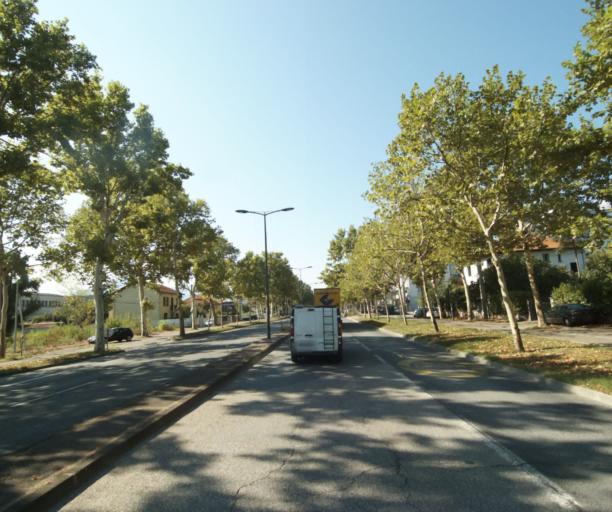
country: FR
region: Rhone-Alpes
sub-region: Departement de l'Isere
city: Le Pont-de-Claix
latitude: 45.1377
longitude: 5.7020
